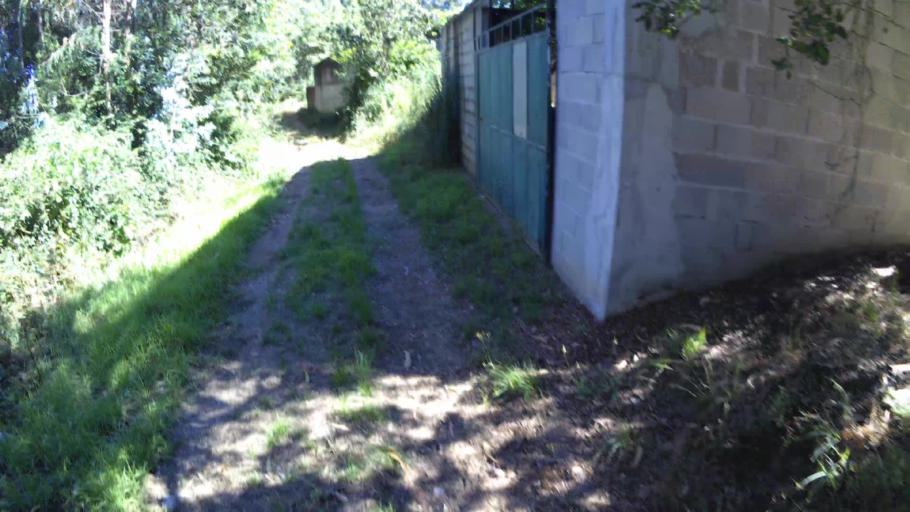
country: PT
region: Aveiro
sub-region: Aveiro
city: Aveiro
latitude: 40.6615
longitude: -8.6204
